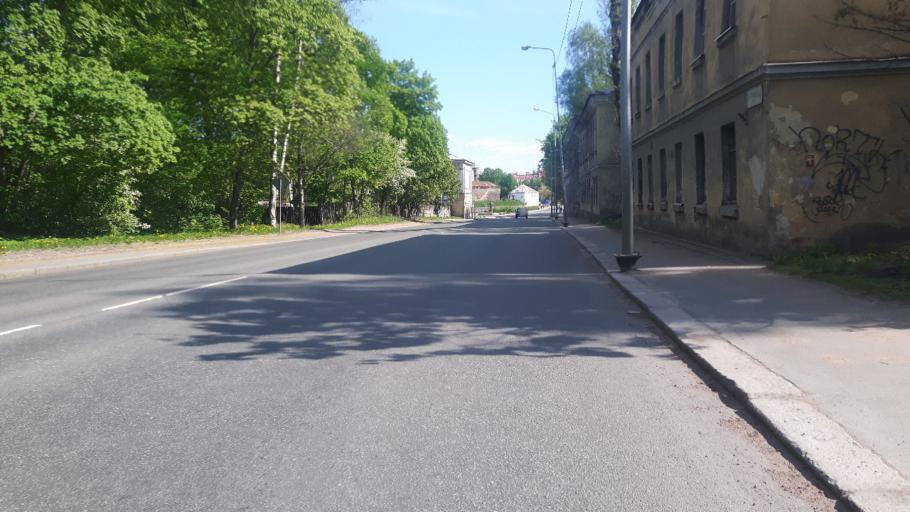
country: RU
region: Leningrad
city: Vyborg
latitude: 60.7184
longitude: 28.7218
